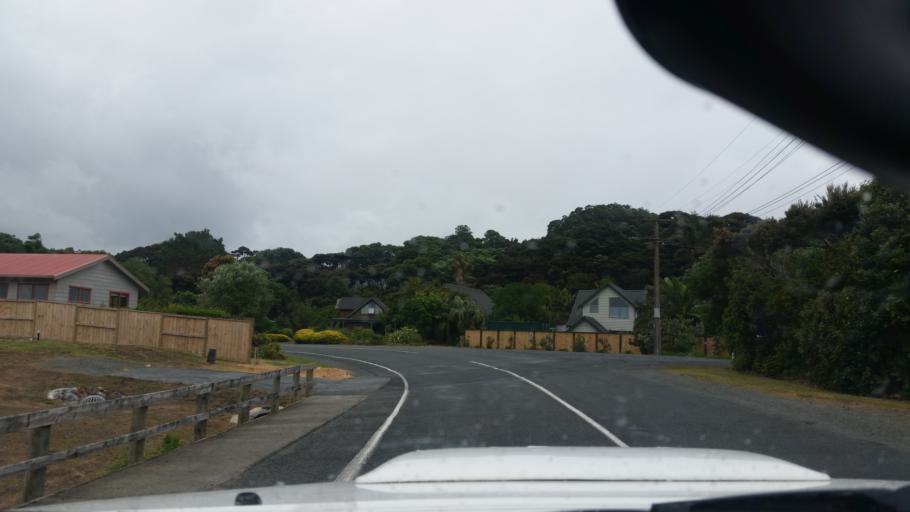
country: NZ
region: Auckland
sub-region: Auckland
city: Wellsford
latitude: -36.1029
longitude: 174.5908
